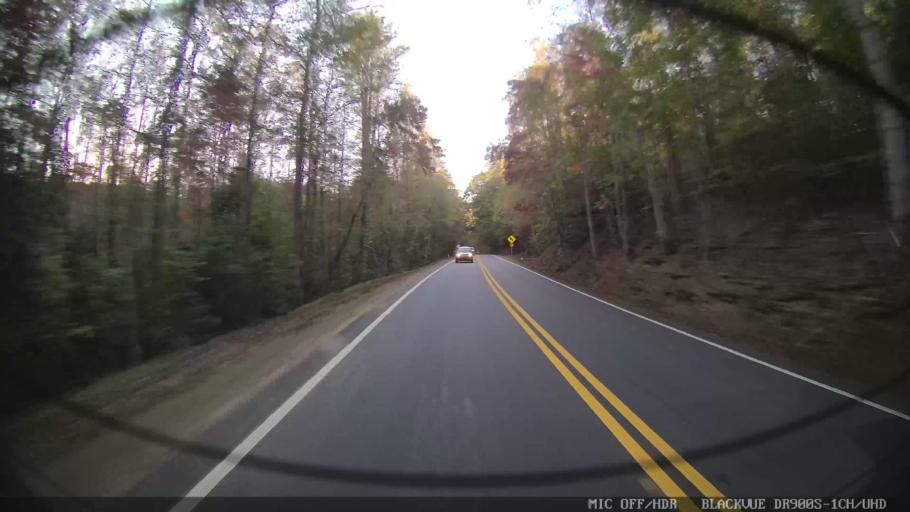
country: US
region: Georgia
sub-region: Lumpkin County
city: Dahlonega
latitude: 34.6264
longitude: -83.9480
